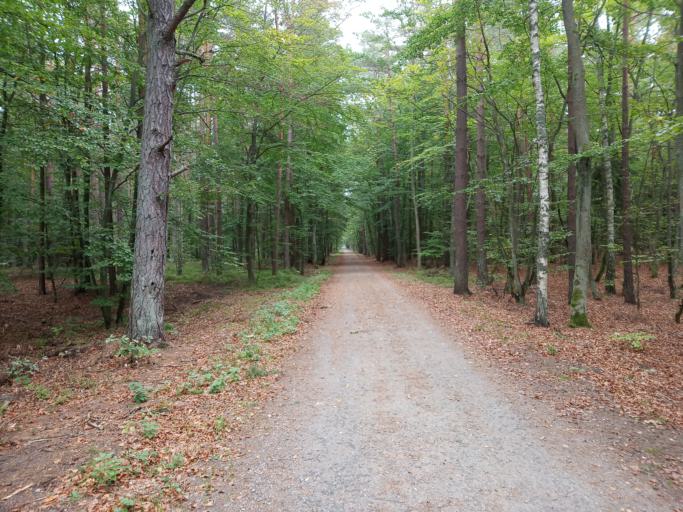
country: PL
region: Pomeranian Voivodeship
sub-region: Powiat nowodworski
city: Stegna
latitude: 54.3375
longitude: 19.1033
